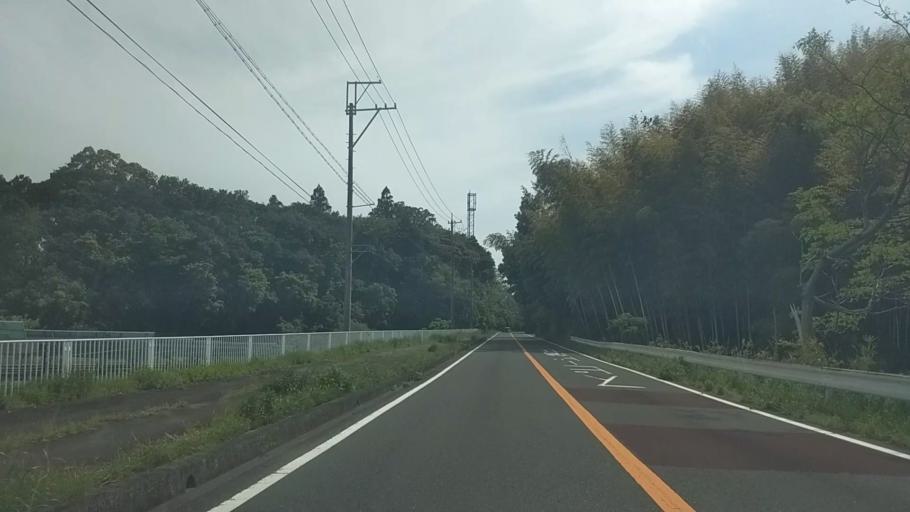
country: JP
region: Shizuoka
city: Kosai-shi
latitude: 34.7376
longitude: 137.6011
